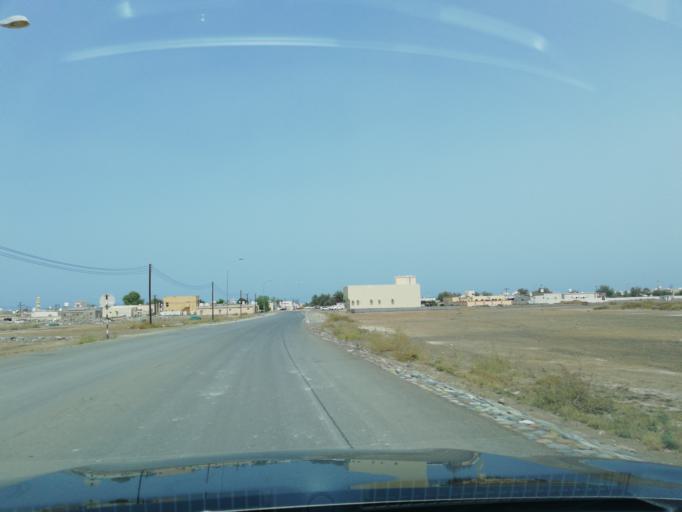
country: OM
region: Al Batinah
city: Shinas
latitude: 24.7392
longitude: 56.4630
